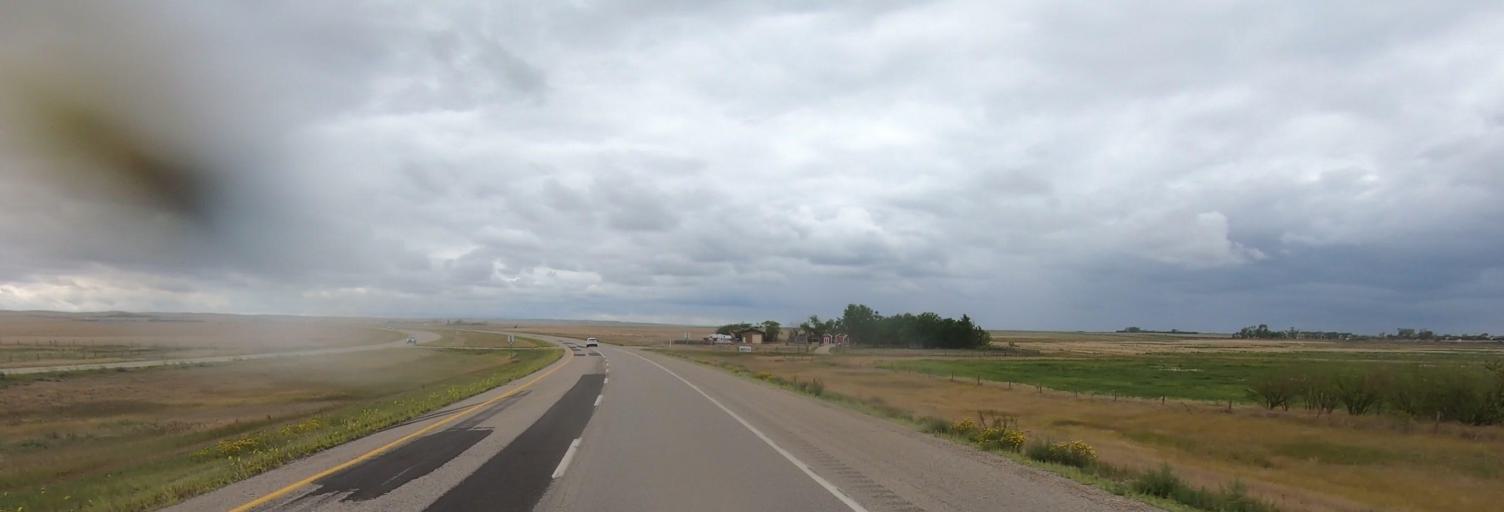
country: CA
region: Saskatchewan
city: Swift Current
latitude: 50.4190
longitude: -107.2401
